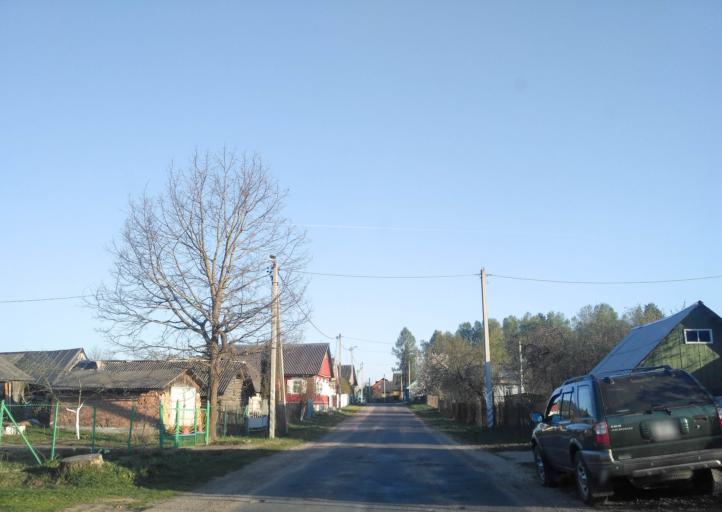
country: BY
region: Minsk
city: Pyatryshki
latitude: 54.1019
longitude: 27.1935
